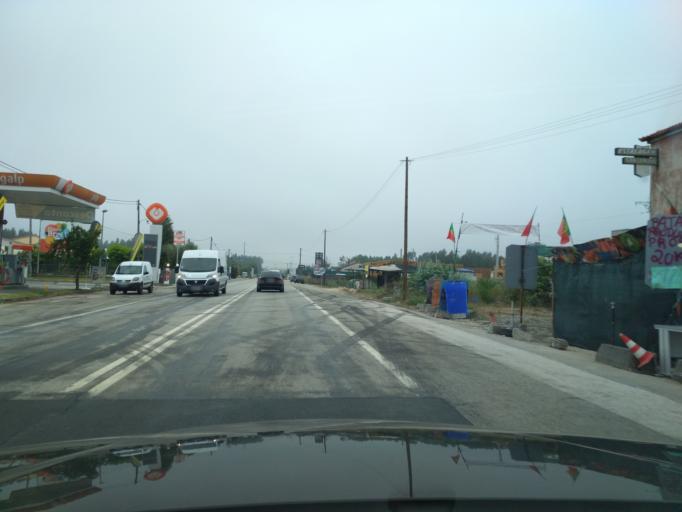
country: PT
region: Aveiro
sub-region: Mealhada
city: Pampilhosa do Botao
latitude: 40.3074
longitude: -8.4489
